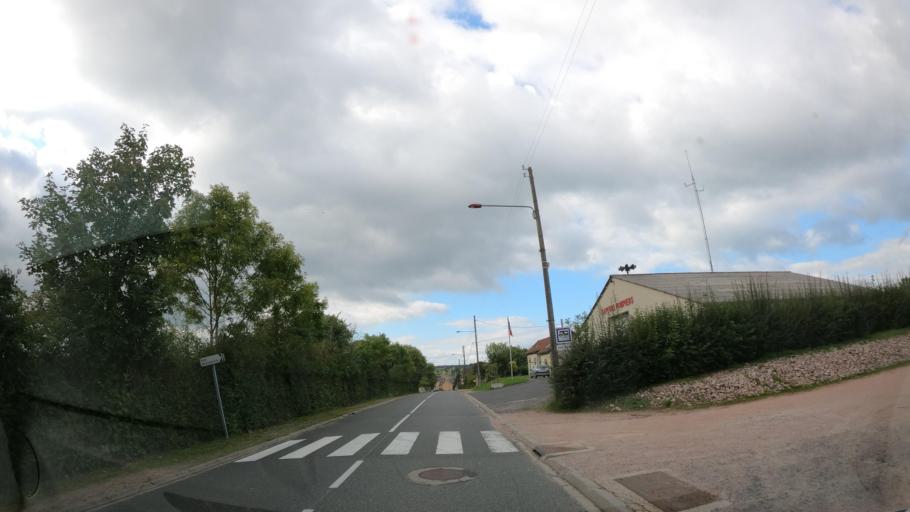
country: FR
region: Auvergne
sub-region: Departement de l'Allier
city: Lapalisse
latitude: 46.3781
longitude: 3.5968
